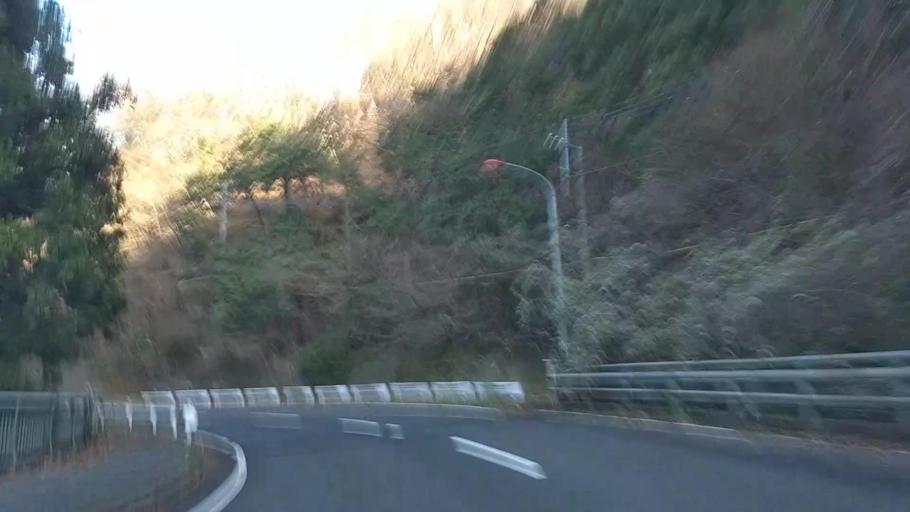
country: JP
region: Yamanashi
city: Uenohara
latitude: 35.5557
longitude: 139.1672
